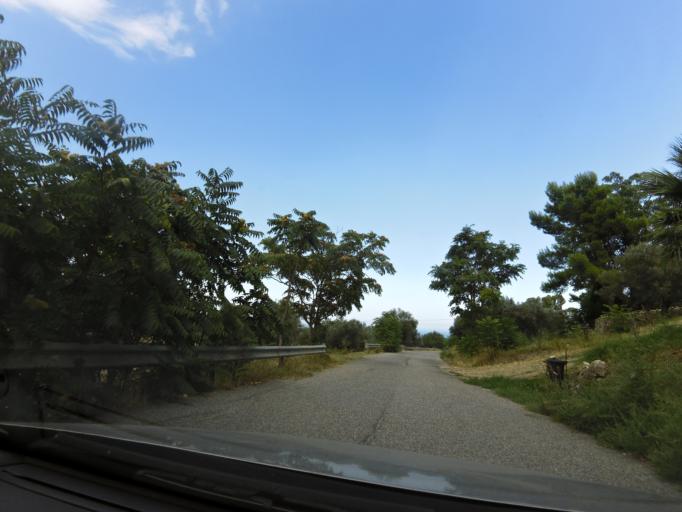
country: IT
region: Calabria
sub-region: Provincia di Reggio Calabria
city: Camini
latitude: 38.4390
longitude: 16.5125
